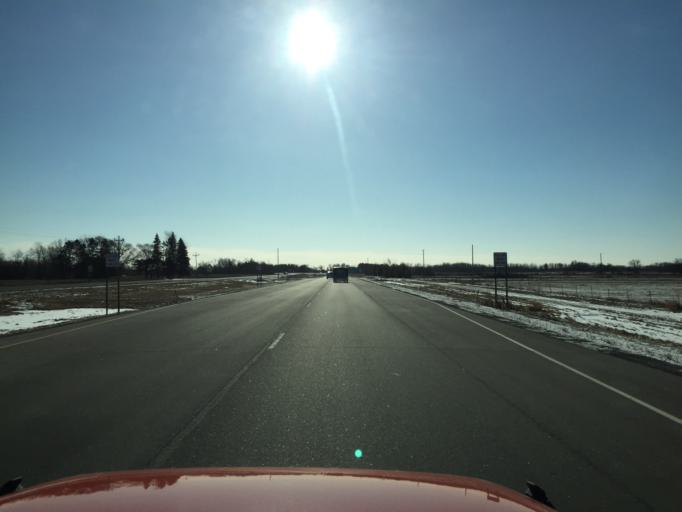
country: US
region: Minnesota
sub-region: Mille Lacs County
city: Milaca
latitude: 45.7951
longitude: -93.6547
